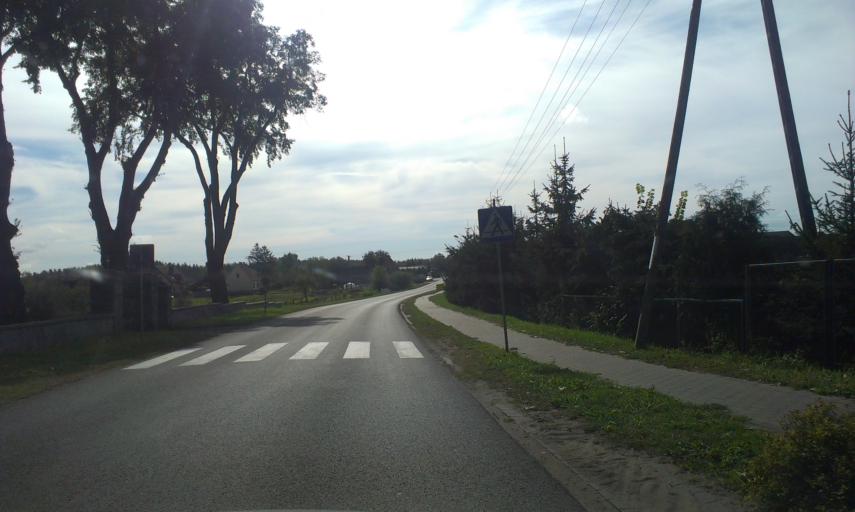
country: PL
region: Greater Poland Voivodeship
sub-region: Powiat zlotowski
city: Zlotow
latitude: 53.4466
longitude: 16.9857
